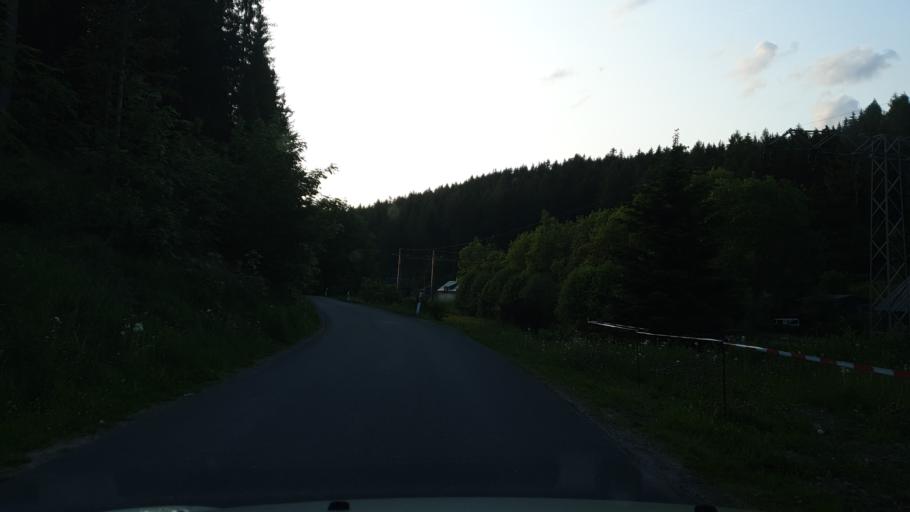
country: DE
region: Saxony
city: Klingenthal
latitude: 50.3829
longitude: 12.4577
